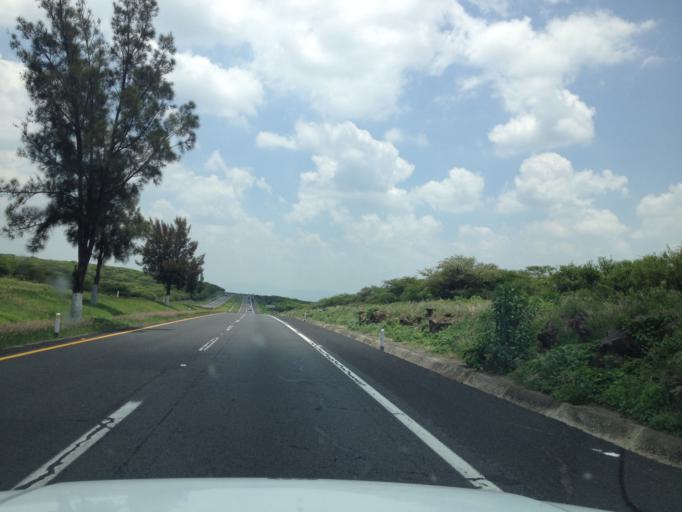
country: MX
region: Michoacan
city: Ixtlan
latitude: 20.2275
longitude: -102.3730
